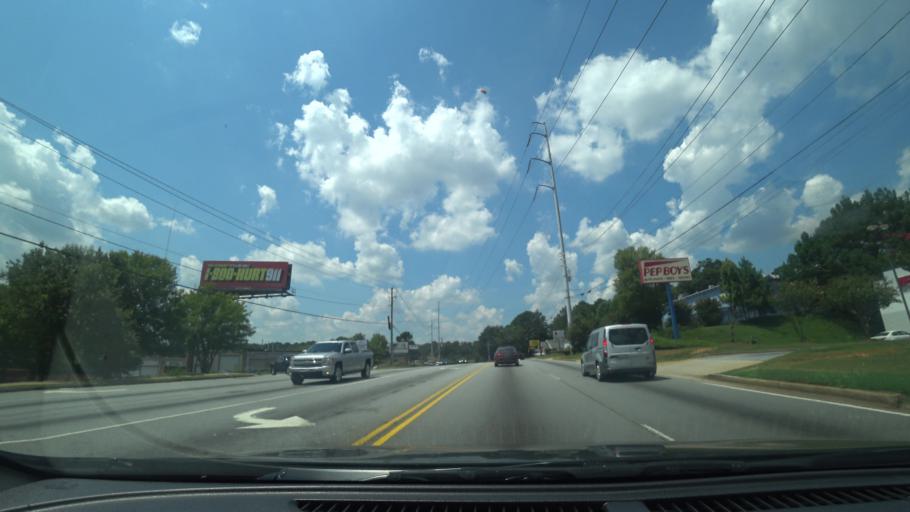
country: US
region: Georgia
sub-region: DeKalb County
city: Redan
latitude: 33.7315
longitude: -84.1949
